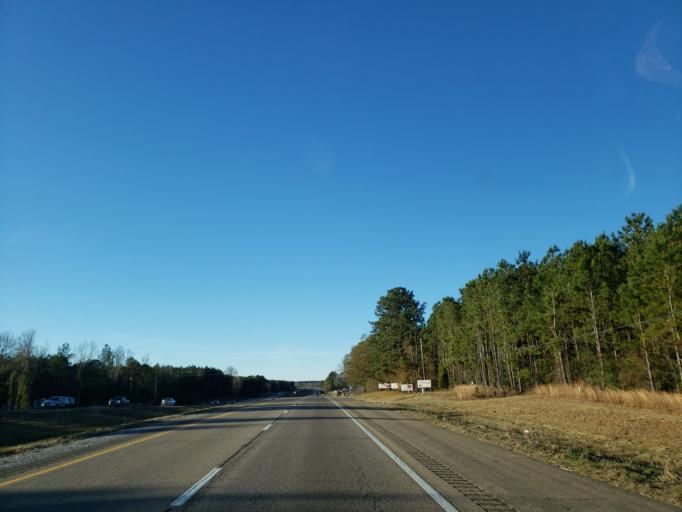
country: US
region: Mississippi
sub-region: Lamar County
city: Sumrall
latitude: 31.4680
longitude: -89.4494
